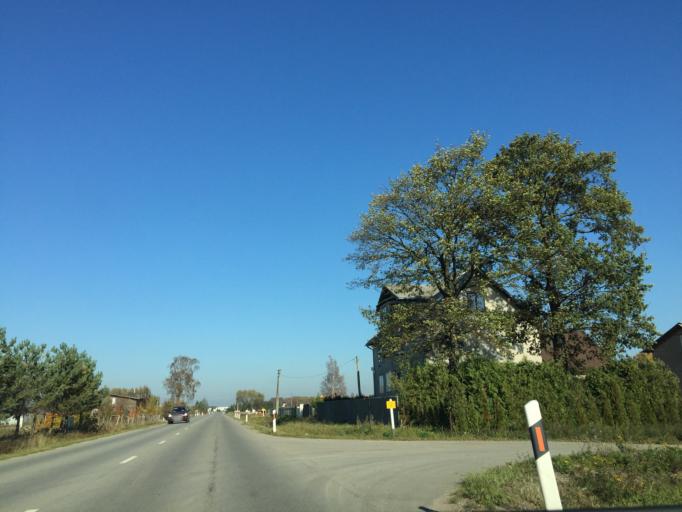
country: LT
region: Klaipedos apskritis
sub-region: Klaipeda
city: Klaipeda
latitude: 55.7505
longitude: 21.1925
